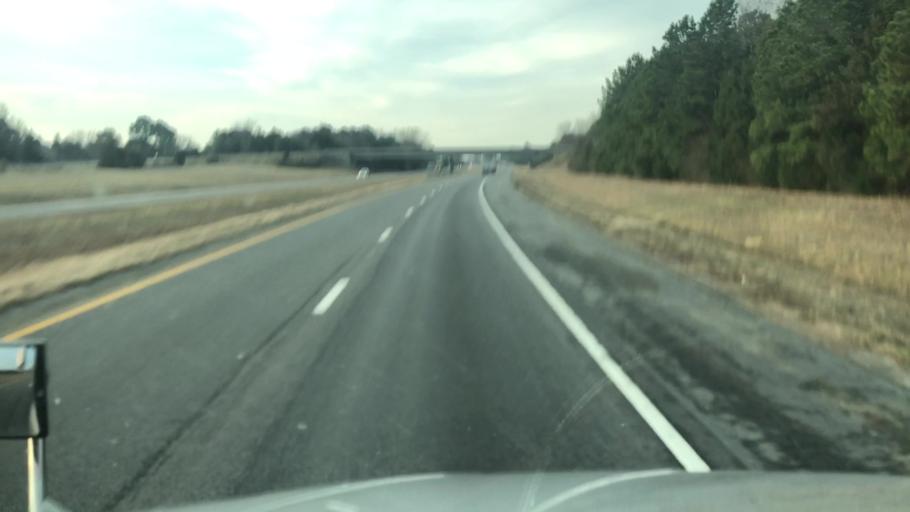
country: US
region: Virginia
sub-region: Sussex County
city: Sussex
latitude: 36.8775
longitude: -77.4043
